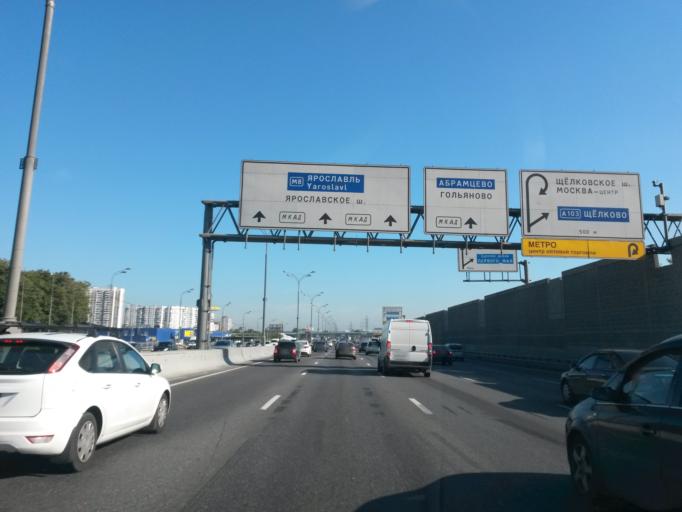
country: RU
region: Moscow
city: Vostochnyy
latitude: 55.8085
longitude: 37.8395
